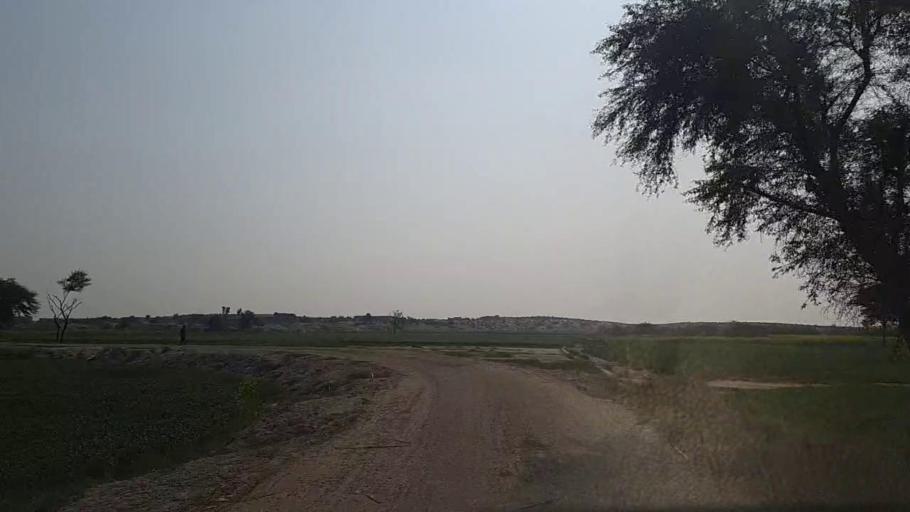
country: PK
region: Sindh
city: Jam Sahib
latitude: 26.4388
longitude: 68.5232
